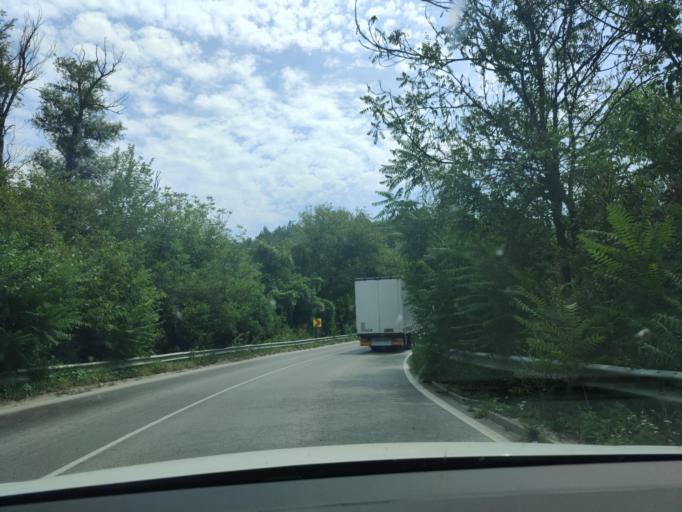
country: BG
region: Vidin
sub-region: Obshtina Dimovo
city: Dimovo
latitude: 43.6788
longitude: 22.7673
